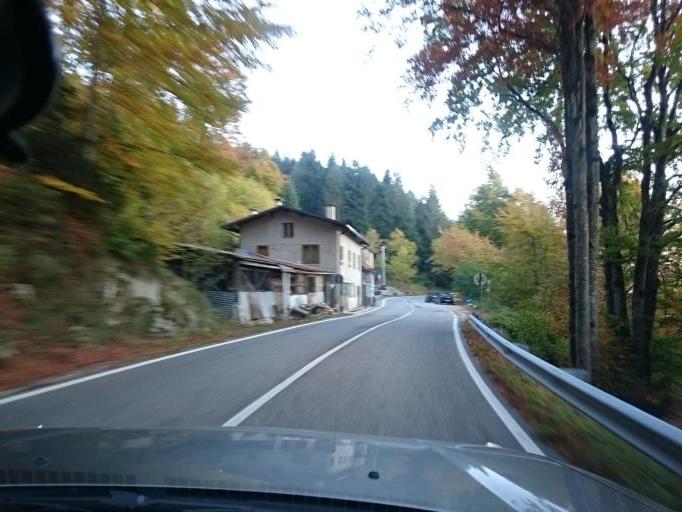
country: IT
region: Veneto
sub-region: Provincia di Vicenza
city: Roana
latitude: 45.8888
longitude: 11.4709
